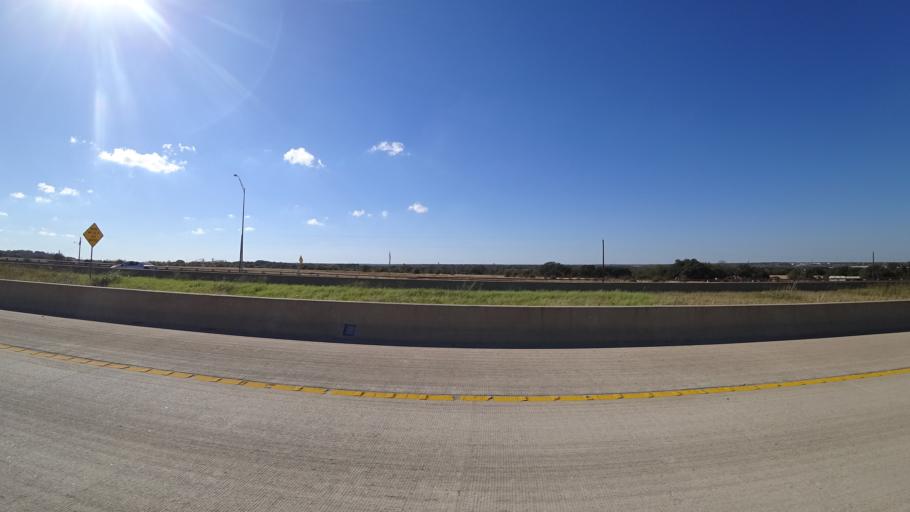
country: US
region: Texas
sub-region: Travis County
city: Wells Branch
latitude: 30.4702
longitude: -97.7020
